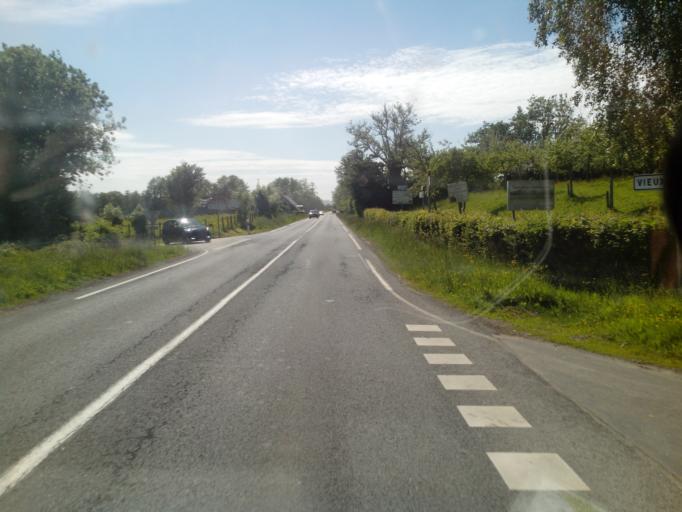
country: FR
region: Lower Normandy
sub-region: Departement du Calvados
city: Saint-Gatien-des-Bois
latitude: 49.3040
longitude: 0.2530
